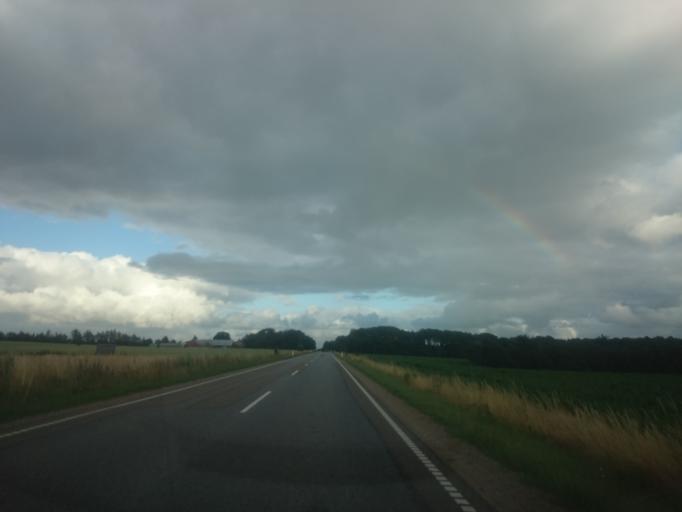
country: DK
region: South Denmark
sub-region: Billund Kommune
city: Grindsted
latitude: 55.6646
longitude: 8.7552
